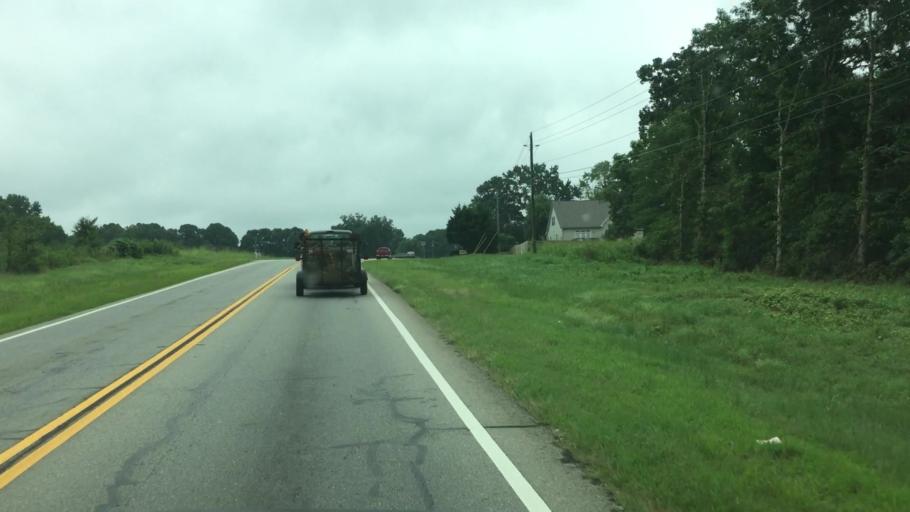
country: US
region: Georgia
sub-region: Jackson County
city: Hoschton
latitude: 34.0494
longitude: -83.7784
